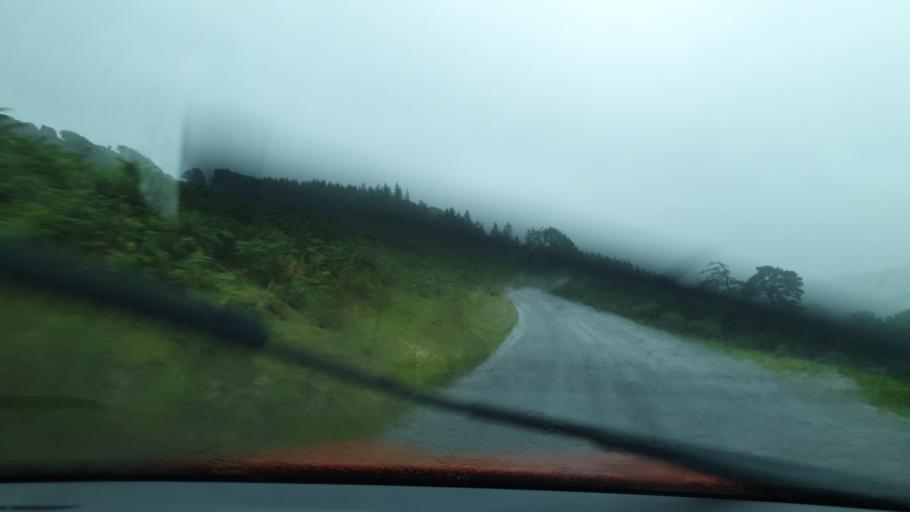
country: GB
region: England
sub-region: Cumbria
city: Millom
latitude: 54.3050
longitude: -3.2284
